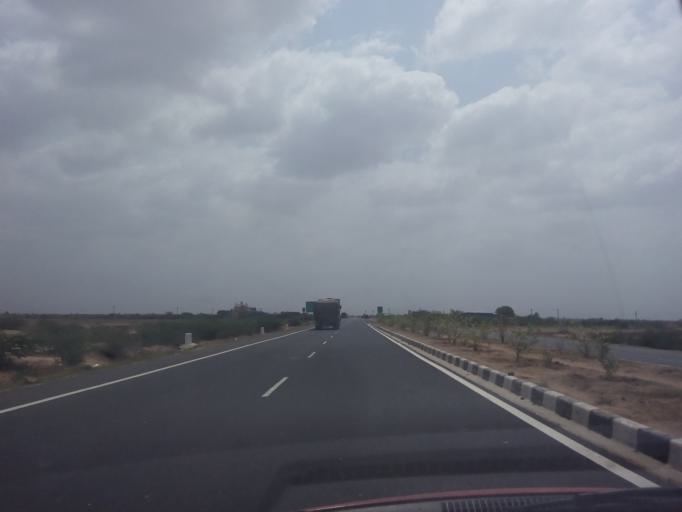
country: IN
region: Gujarat
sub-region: Surendranagar
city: Lakhtar
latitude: 23.0484
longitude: 71.7103
